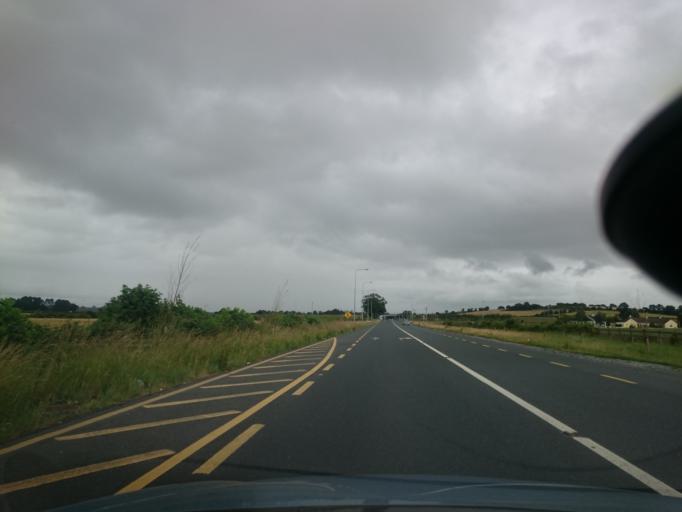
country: IE
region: Leinster
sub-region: Kildare
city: Castledermot
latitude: 52.8870
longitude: -6.8646
